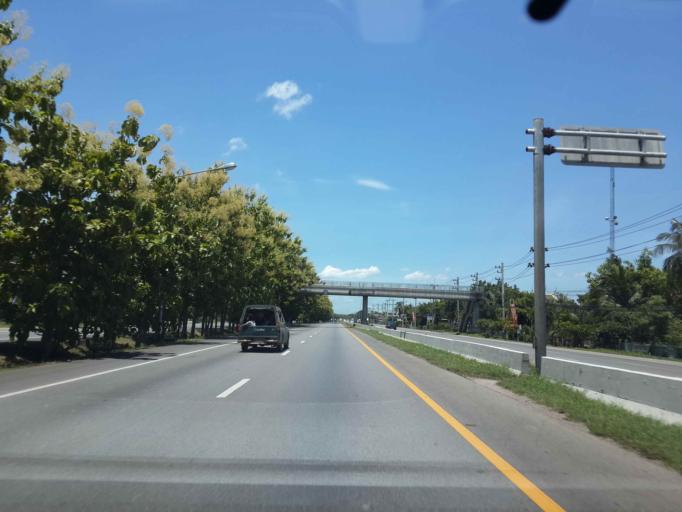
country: TH
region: Phetchaburi
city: Khao Yoi
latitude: 13.1950
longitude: 99.8314
